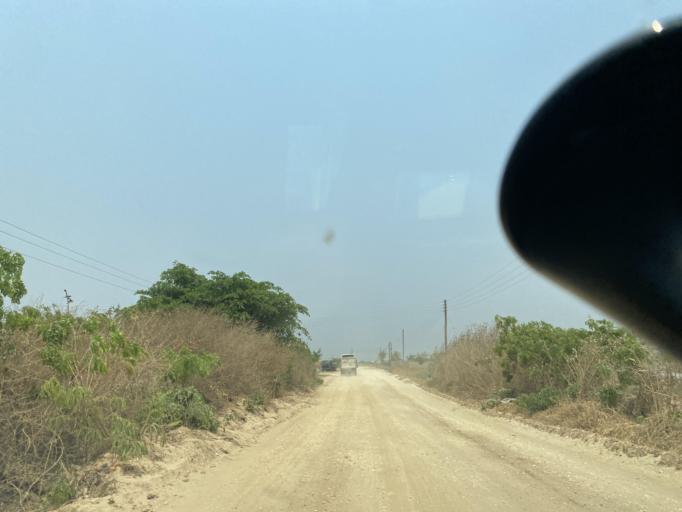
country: ZM
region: Lusaka
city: Lusaka
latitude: -15.5370
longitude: 28.3500
